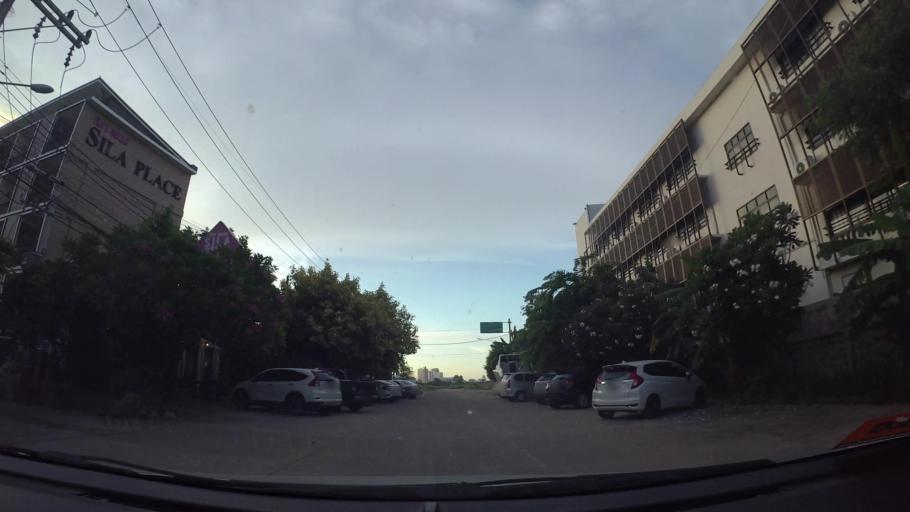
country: TH
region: Chon Buri
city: Phatthaya
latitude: 12.9112
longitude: 100.8893
